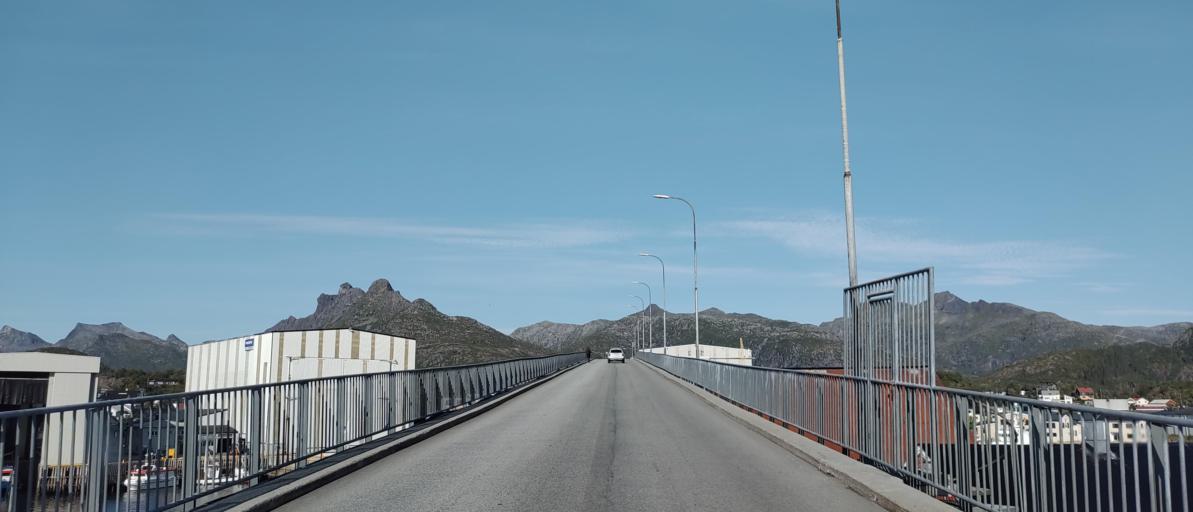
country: NO
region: Nordland
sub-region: Vagan
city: Svolvaer
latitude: 68.2353
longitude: 14.5785
